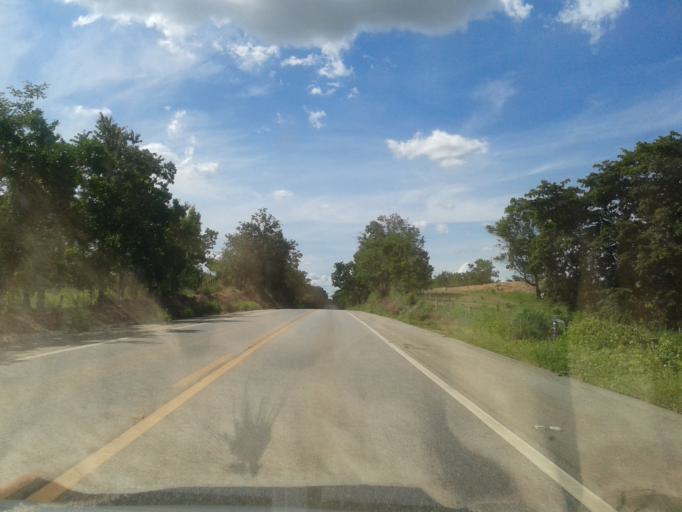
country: BR
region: Goias
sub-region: Itapuranga
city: Itapuranga
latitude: -15.4814
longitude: -50.3320
